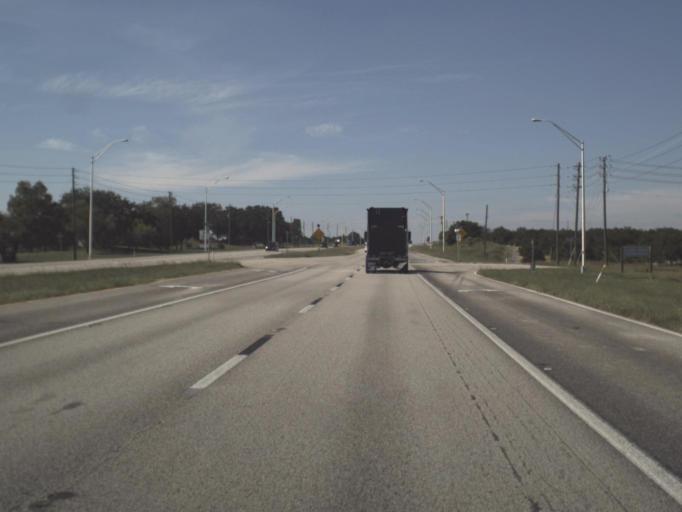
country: US
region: Florida
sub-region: Highlands County
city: Lake Placid
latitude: 27.3203
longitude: -81.3667
